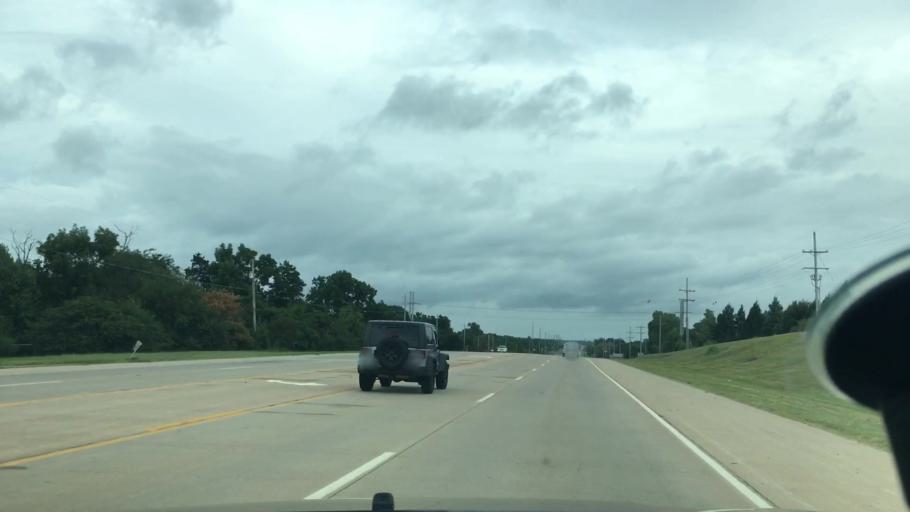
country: US
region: Oklahoma
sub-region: Seminole County
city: Seminole
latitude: 35.2674
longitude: -96.6710
